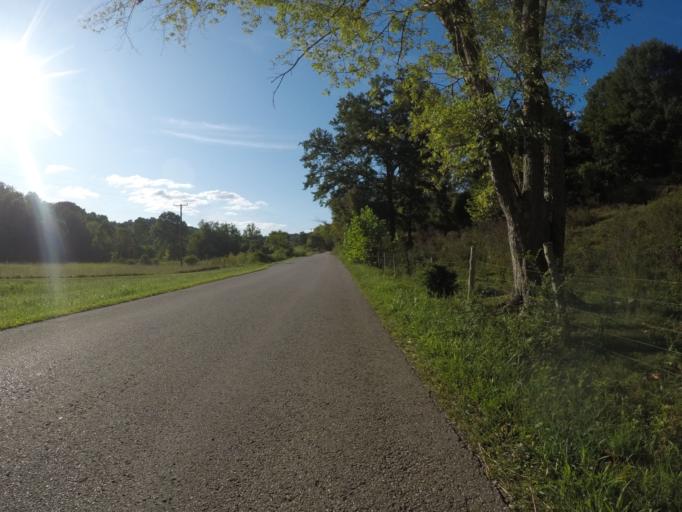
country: US
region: West Virginia
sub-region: Cabell County
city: Huntington
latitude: 38.5125
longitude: -82.4969
